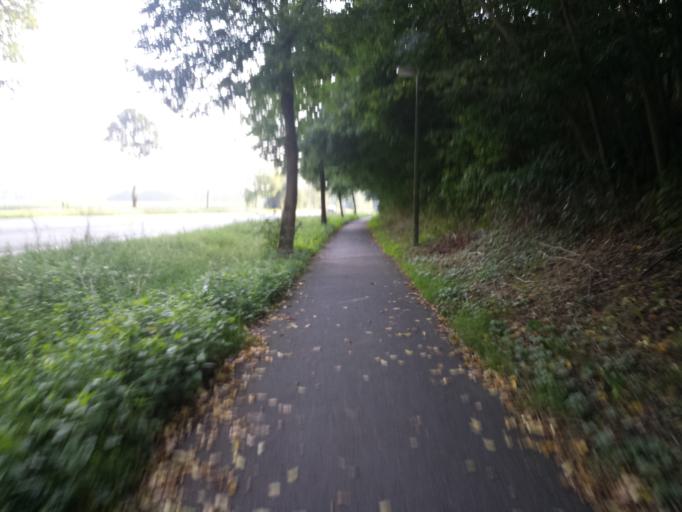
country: DE
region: North Rhine-Westphalia
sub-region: Regierungsbezirk Detmold
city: Rheda-Wiedenbruck
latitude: 51.9014
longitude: 8.3196
